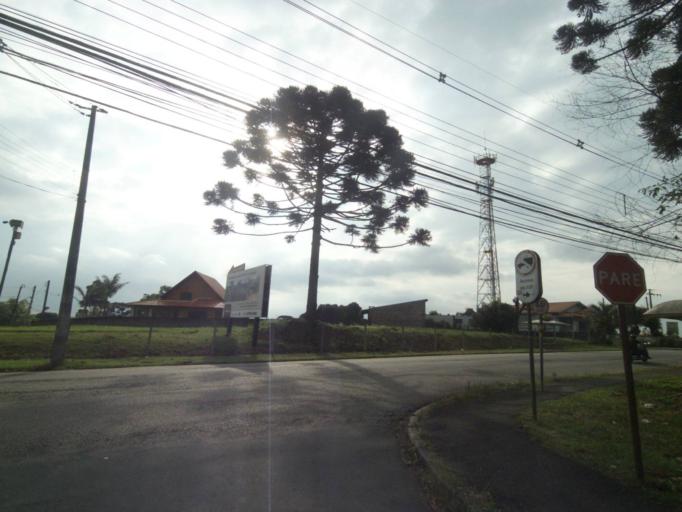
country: BR
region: Parana
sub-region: Curitiba
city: Curitiba
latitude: -25.4077
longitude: -49.3130
